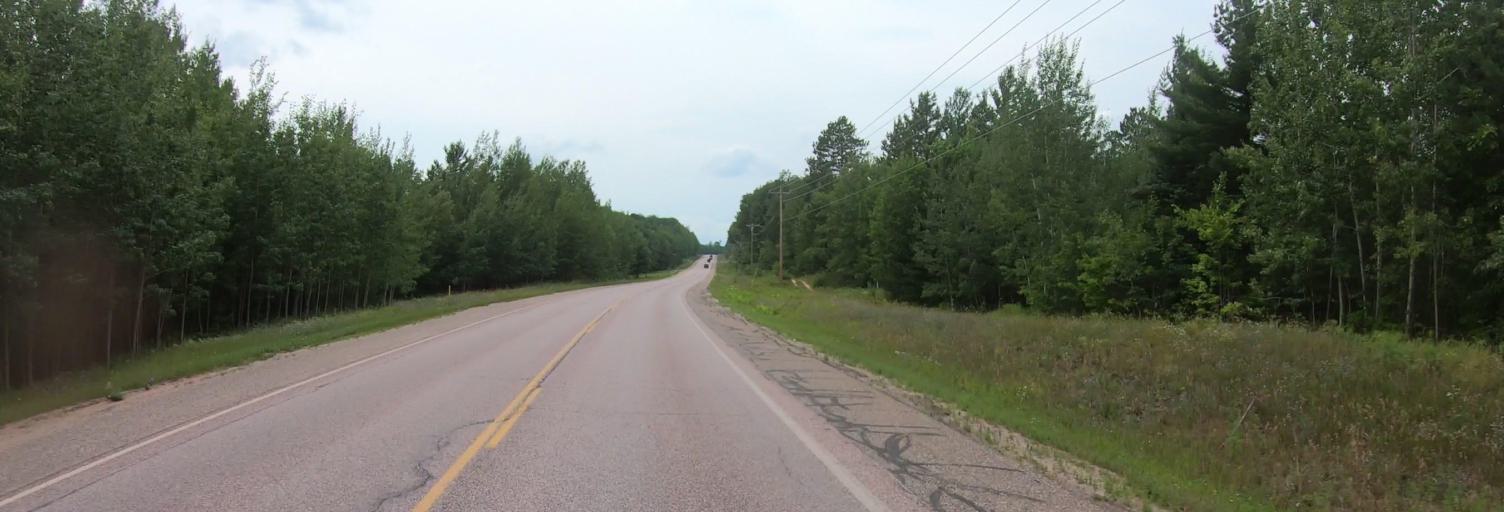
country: US
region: Michigan
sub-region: Marquette County
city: Harvey
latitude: 46.4604
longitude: -87.3946
